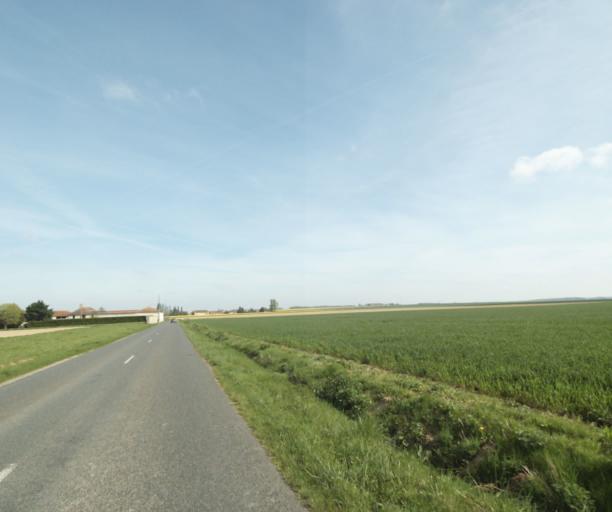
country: FR
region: Ile-de-France
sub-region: Departement de Seine-et-Marne
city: Bailly-Carrois
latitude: 48.5773
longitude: 3.0118
